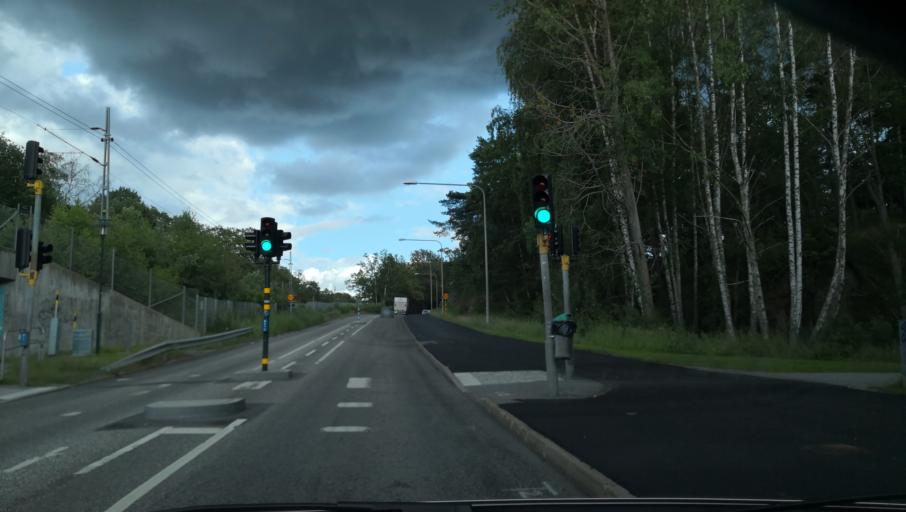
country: SE
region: Stockholm
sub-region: Stockholms Kommun
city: Arsta
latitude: 59.2399
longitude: 18.0879
